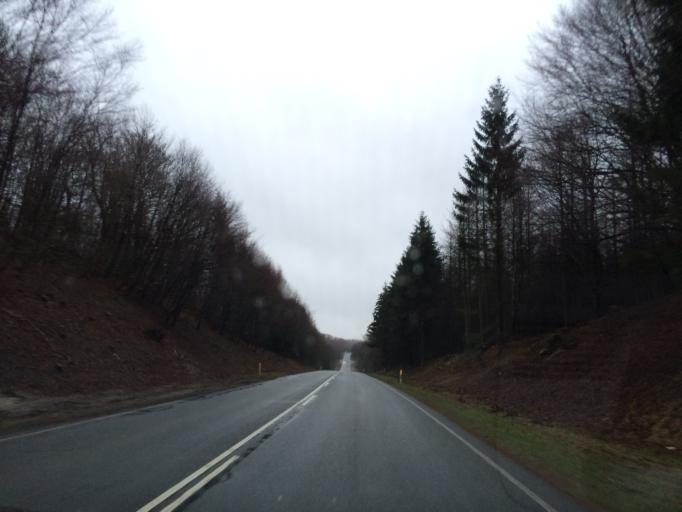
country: DK
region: North Denmark
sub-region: Mariagerfjord Kommune
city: Arden
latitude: 56.8014
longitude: 9.8175
